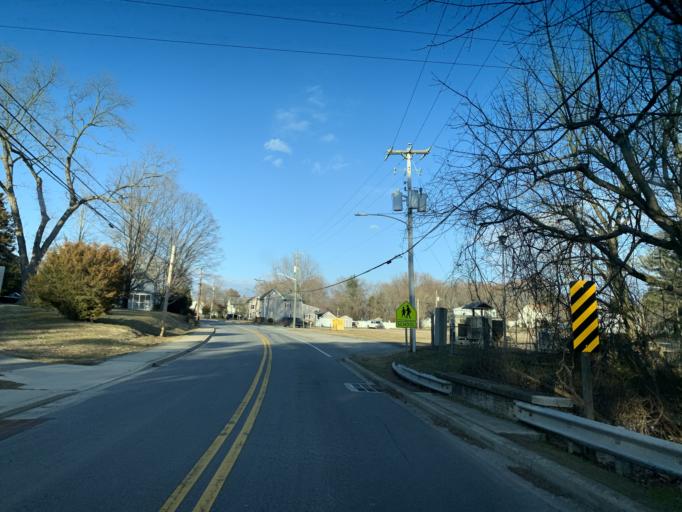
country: US
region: Maryland
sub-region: Queen Anne's County
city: Kingstown
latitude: 39.1450
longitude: -75.9816
